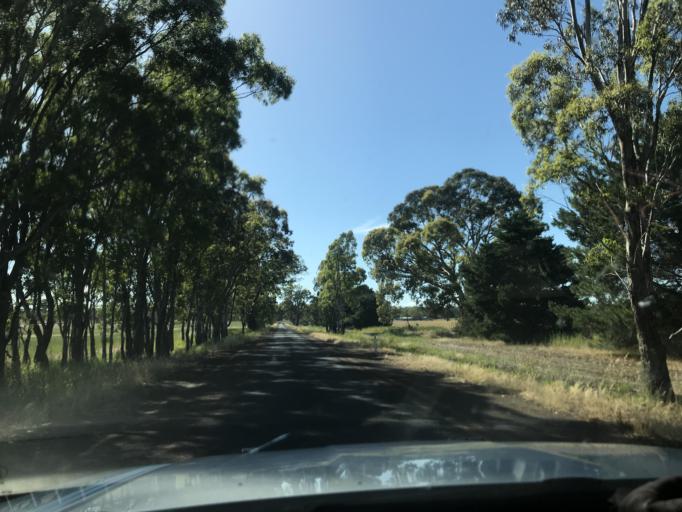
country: AU
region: Victoria
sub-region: Horsham
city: Horsham
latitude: -37.0890
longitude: 141.7633
